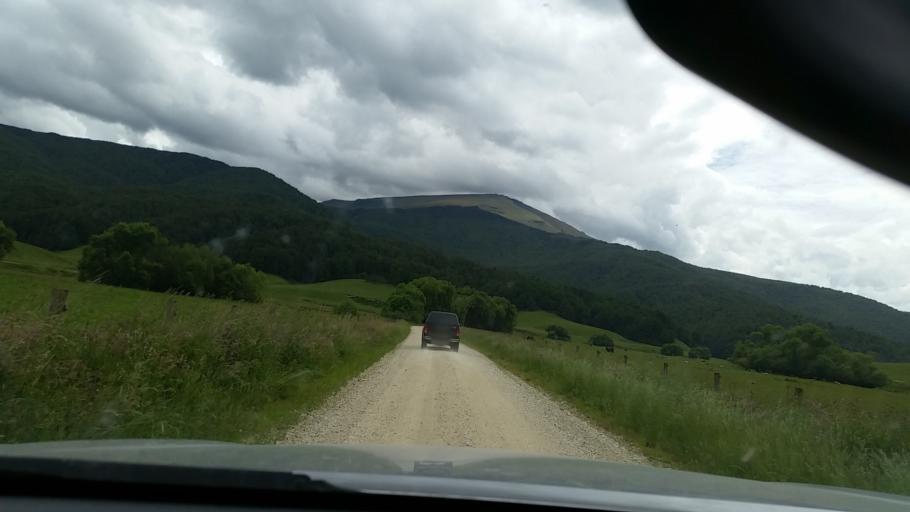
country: NZ
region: Otago
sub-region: Queenstown-Lakes District
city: Kingston
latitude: -45.5803
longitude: 169.0020
